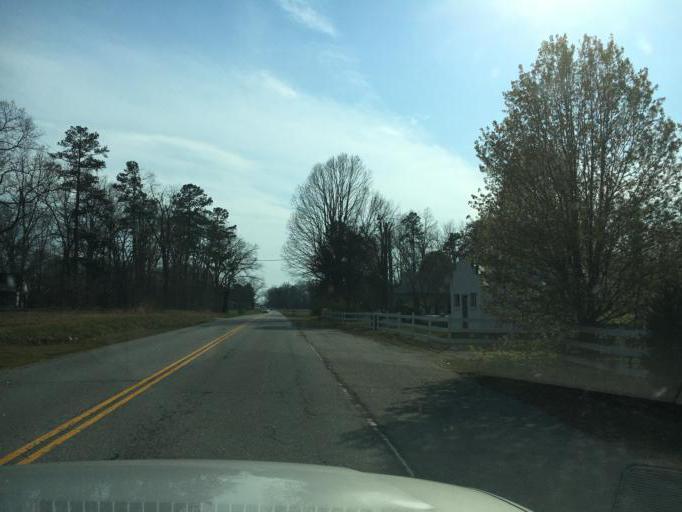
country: US
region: South Carolina
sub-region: Spartanburg County
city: Mayo
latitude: 35.1615
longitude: -81.8470
